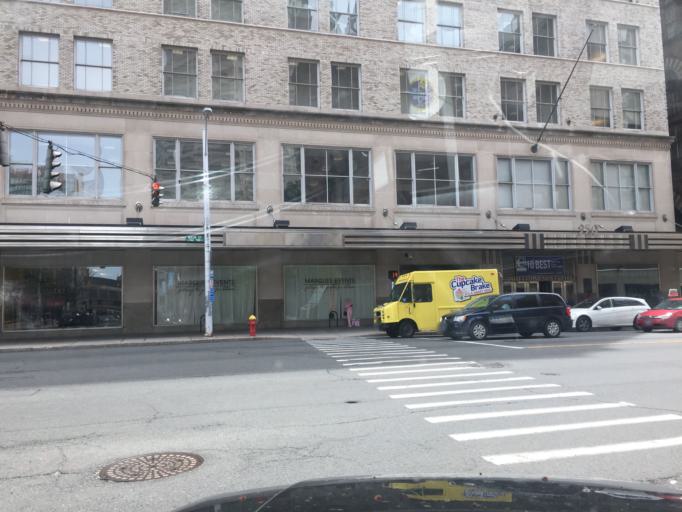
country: US
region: Connecticut
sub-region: Hartford County
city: Hartford
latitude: 41.7685
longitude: -72.6733
